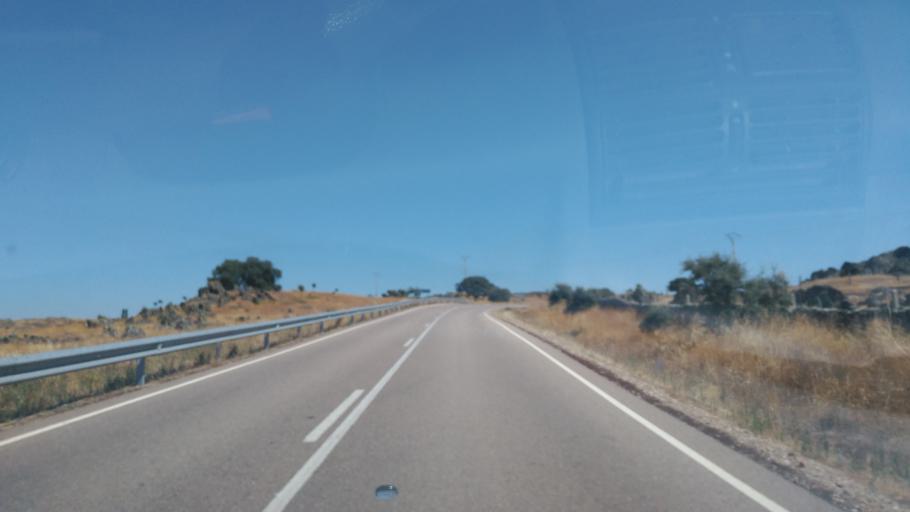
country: ES
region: Castille and Leon
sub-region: Provincia de Salamanca
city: Berrocal de Huebra
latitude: 40.7116
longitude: -6.0059
